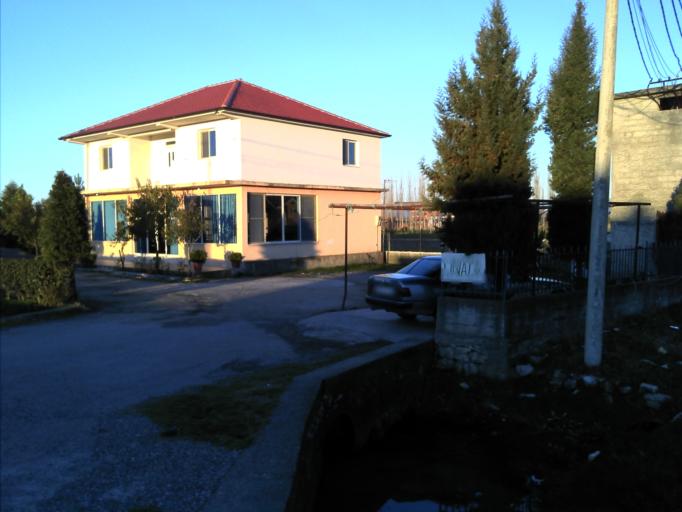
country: AL
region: Shkoder
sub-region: Rrethi i Shkodres
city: Berdica e Madhe
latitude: 41.9826
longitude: 19.4804
